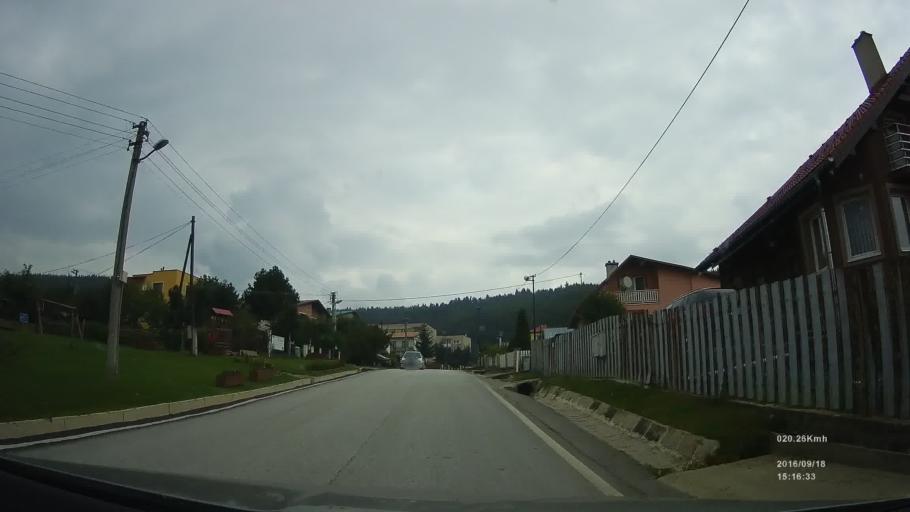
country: SK
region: Presovsky
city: Lubica
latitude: 49.0204
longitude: 20.4845
